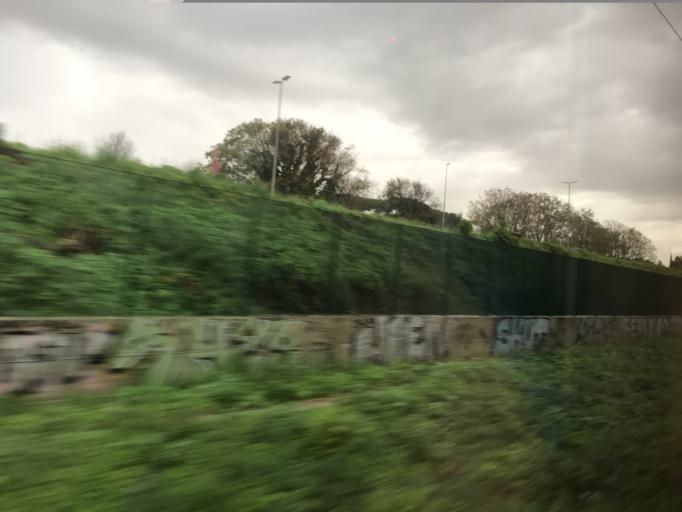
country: IT
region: Latium
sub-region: Citta metropolitana di Roma Capitale
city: Rome
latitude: 41.8709
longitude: 12.4986
